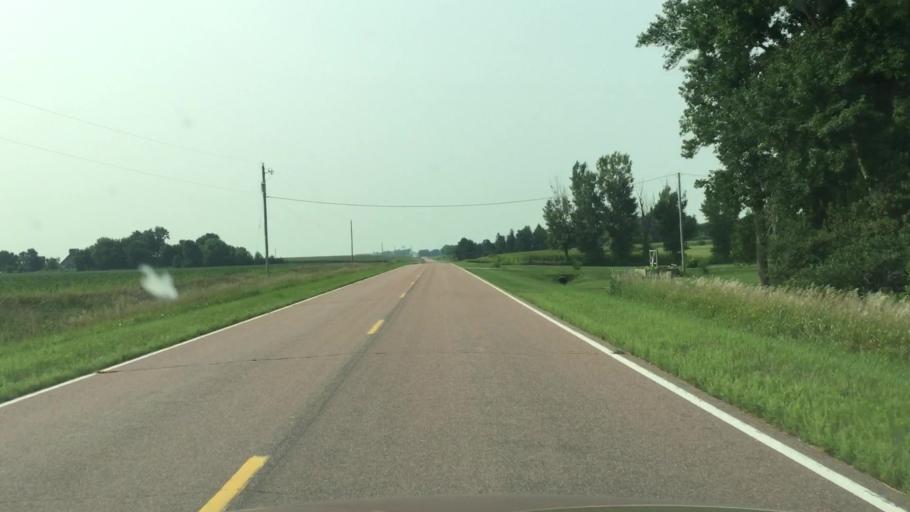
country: US
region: Iowa
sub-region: O'Brien County
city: Sheldon
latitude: 43.2492
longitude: -95.7833
